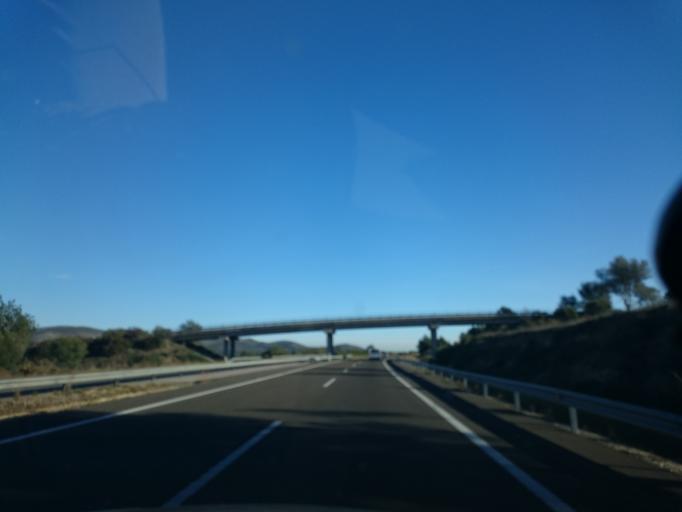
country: ES
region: Valencia
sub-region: Provincia de Castello
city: Santa Magdalena de Pulpis
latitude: 40.3410
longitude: 0.2720
